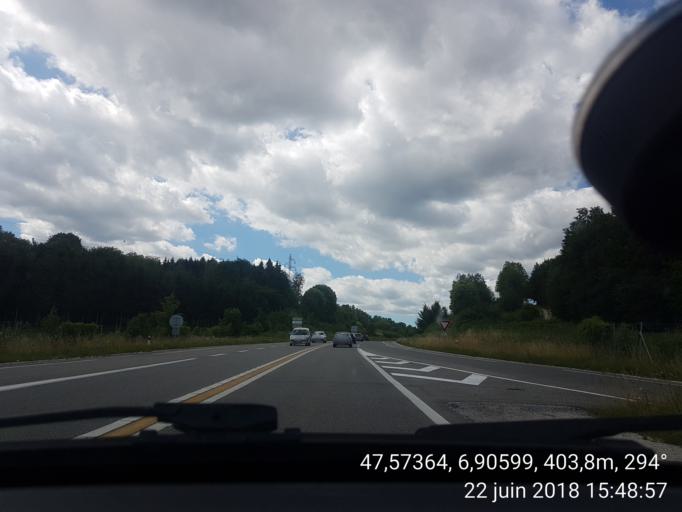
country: FR
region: Franche-Comte
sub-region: Territoire de Belfort
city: Bourogne
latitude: 47.5735
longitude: 6.9061
